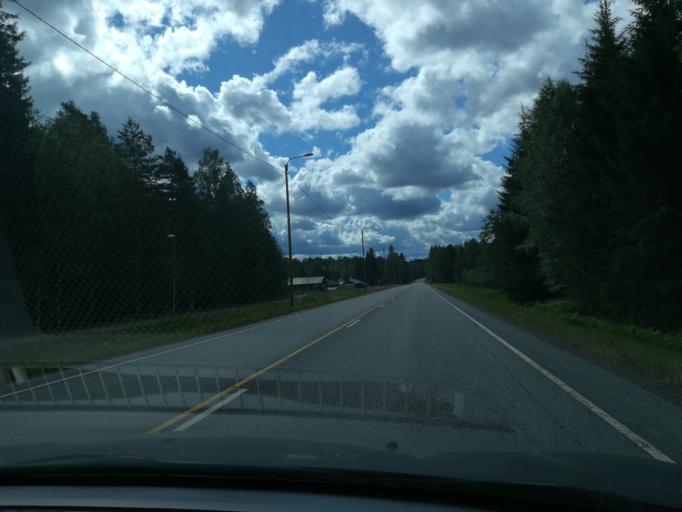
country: FI
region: Southern Savonia
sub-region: Mikkeli
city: Ristiina
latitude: 61.4805
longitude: 27.2515
